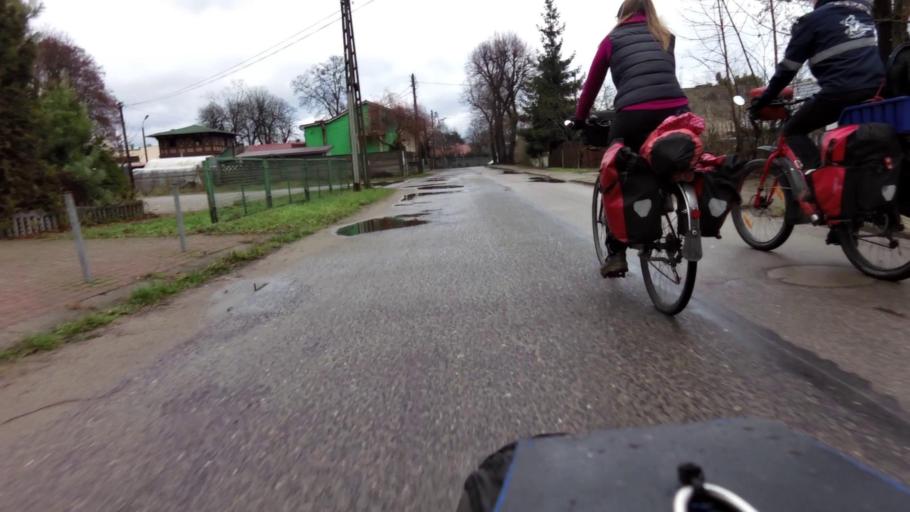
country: PL
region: Lubusz
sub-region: Powiat gorzowski
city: Witnica
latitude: 52.6844
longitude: 14.8870
